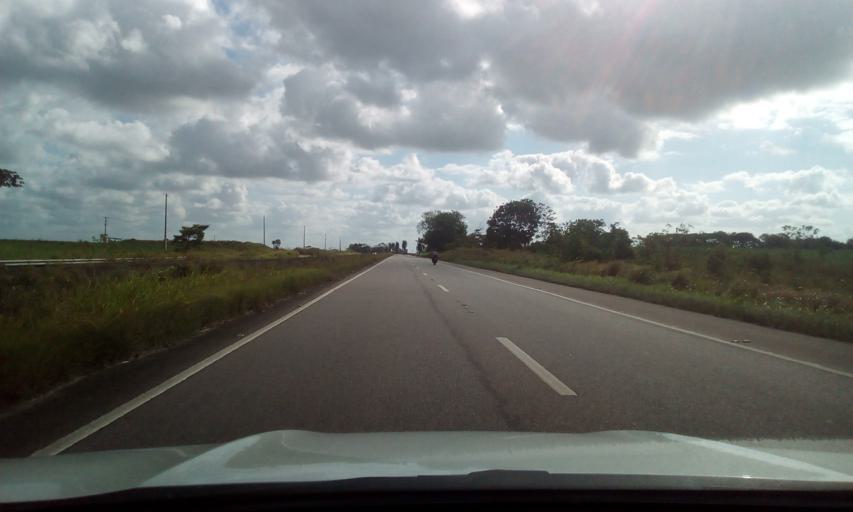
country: BR
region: Pernambuco
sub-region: Itapissuma
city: Itapissuma
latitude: -7.7168
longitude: -34.9375
